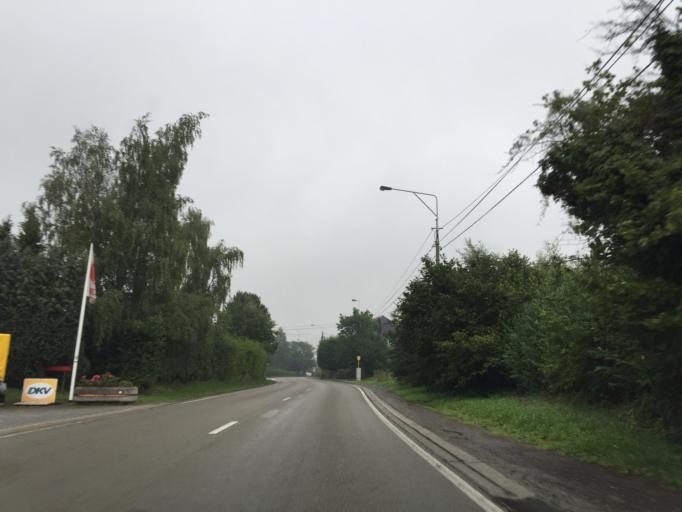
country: BE
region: Wallonia
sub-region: Province de Liege
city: Spa
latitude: 50.5151
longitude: 5.9088
